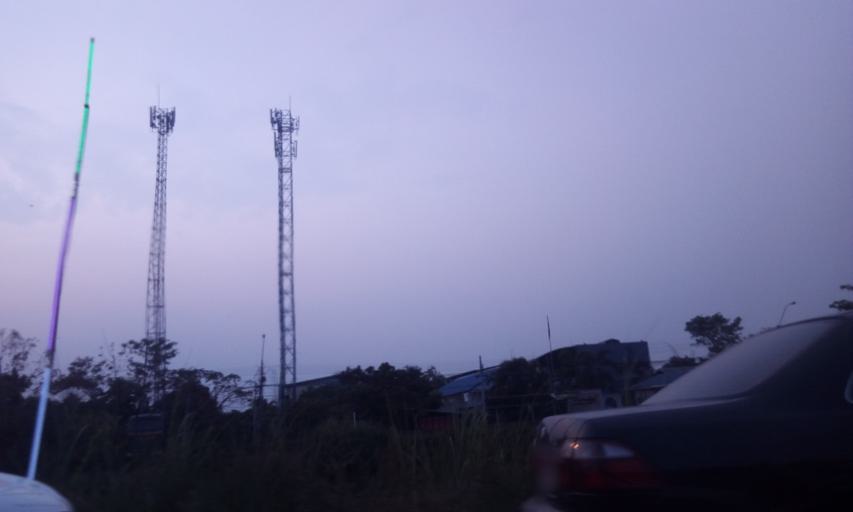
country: TH
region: Bangkok
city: Nong Chok
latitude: 13.8750
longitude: 100.8836
